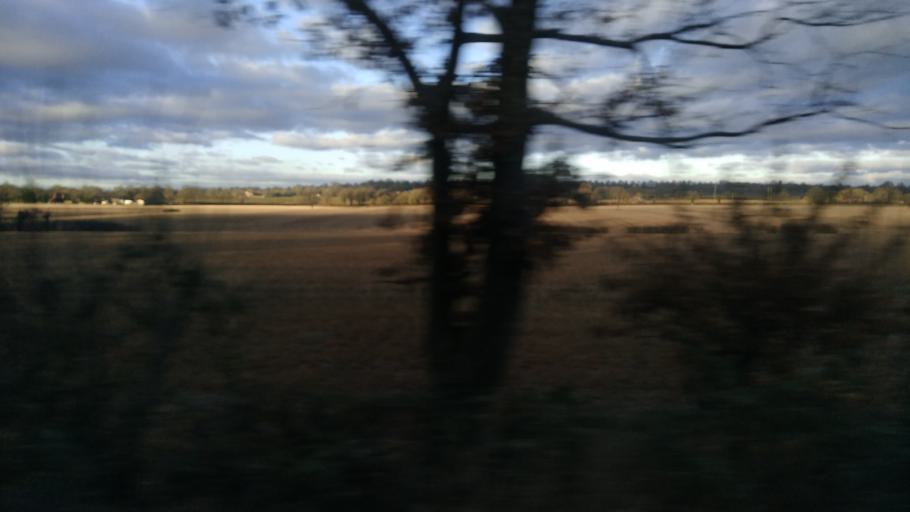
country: GB
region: England
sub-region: Kent
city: Lenham
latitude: 51.1560
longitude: 0.7533
